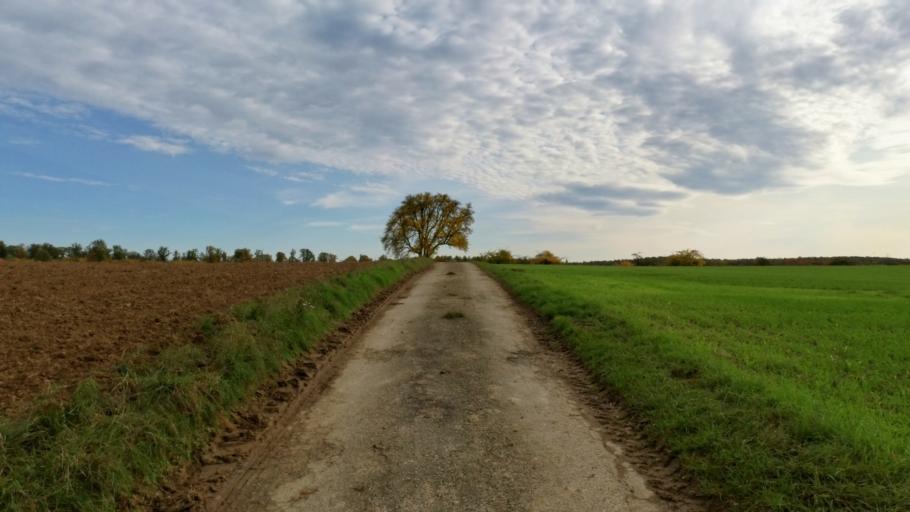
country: DE
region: Baden-Wuerttemberg
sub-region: Karlsruhe Region
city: Binau
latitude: 49.3760
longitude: 9.0381
